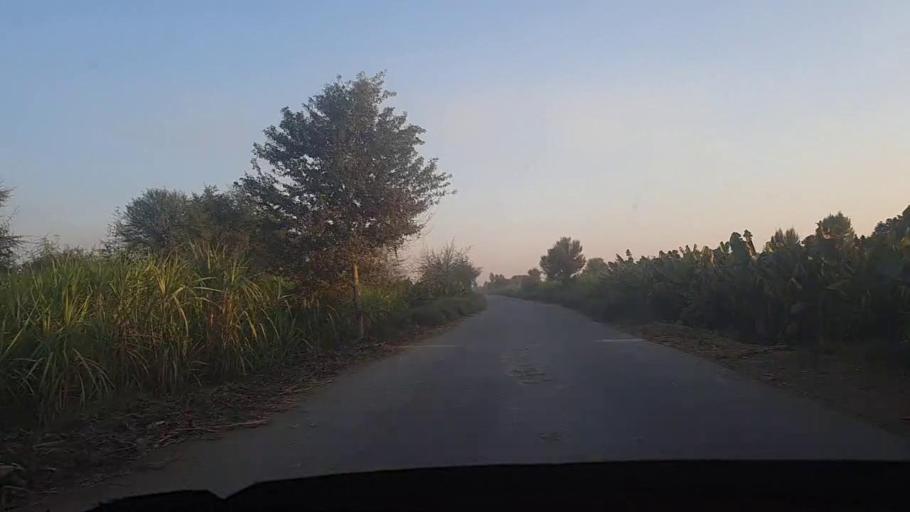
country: PK
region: Sindh
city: Sobhadero
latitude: 27.3465
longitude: 68.3762
